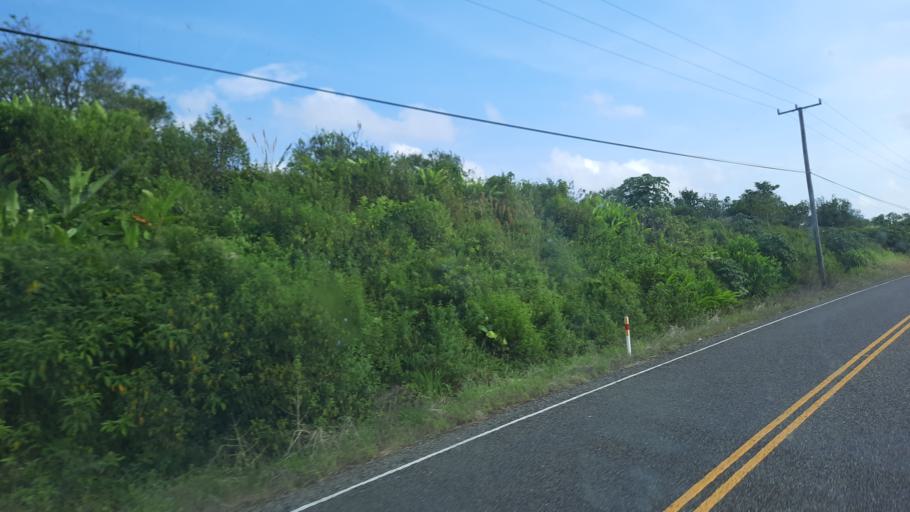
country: BZ
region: Cayo
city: Belmopan
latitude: 17.1152
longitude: -88.6566
